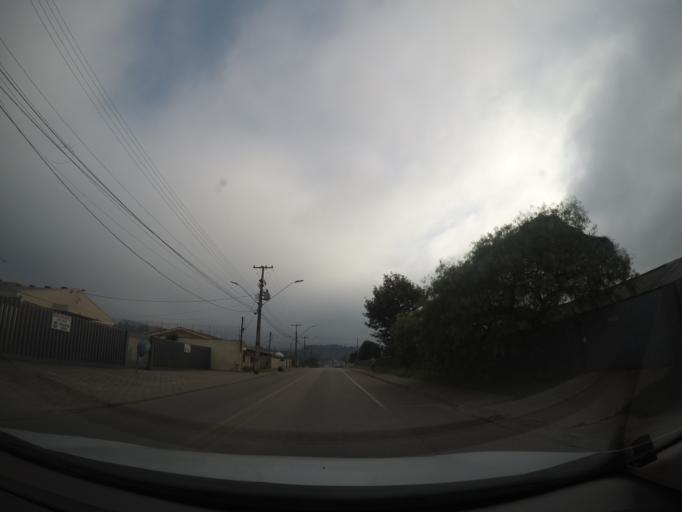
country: BR
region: Parana
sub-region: Colombo
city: Colombo
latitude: -25.2930
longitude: -49.2307
